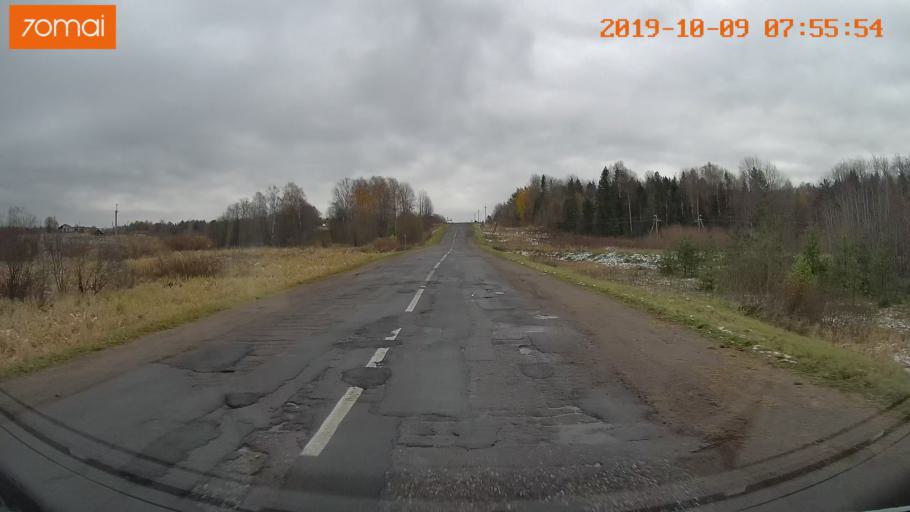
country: RU
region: Jaroslavl
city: Kukoboy
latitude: 58.6989
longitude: 39.9277
